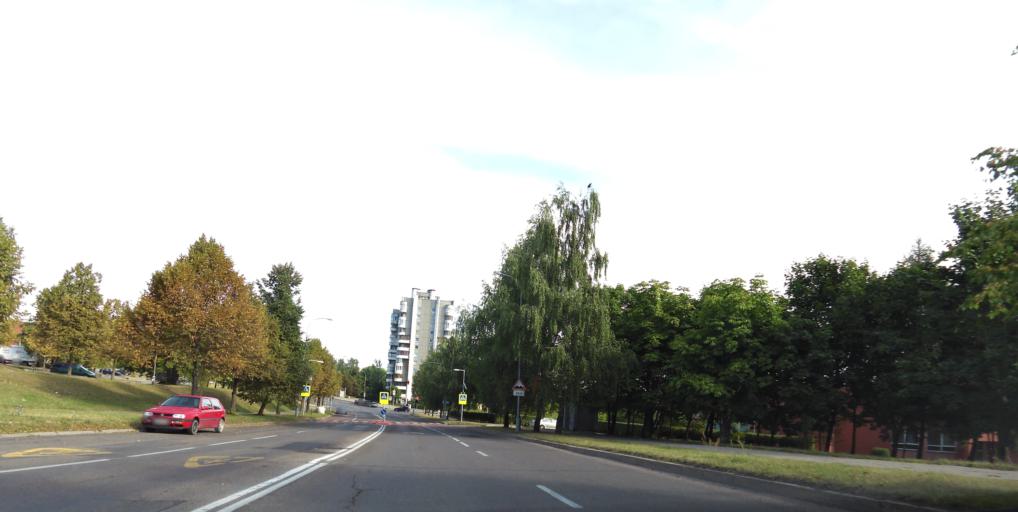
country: LT
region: Vilnius County
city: Seskine
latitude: 54.7146
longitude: 25.2517
